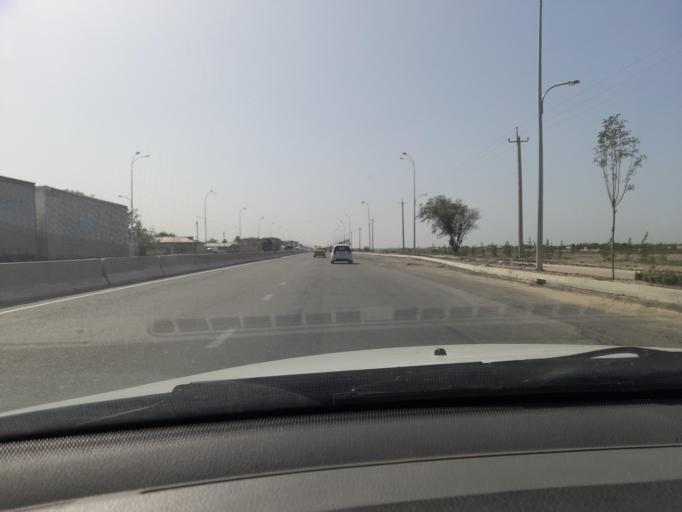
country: UZ
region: Samarqand
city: Samarqand
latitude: 39.7078
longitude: 66.9889
